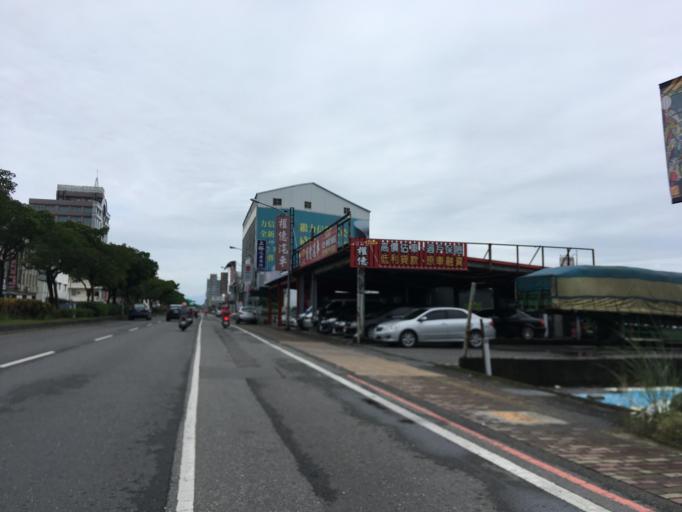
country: TW
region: Taiwan
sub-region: Yilan
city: Yilan
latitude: 24.7013
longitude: 121.7697
